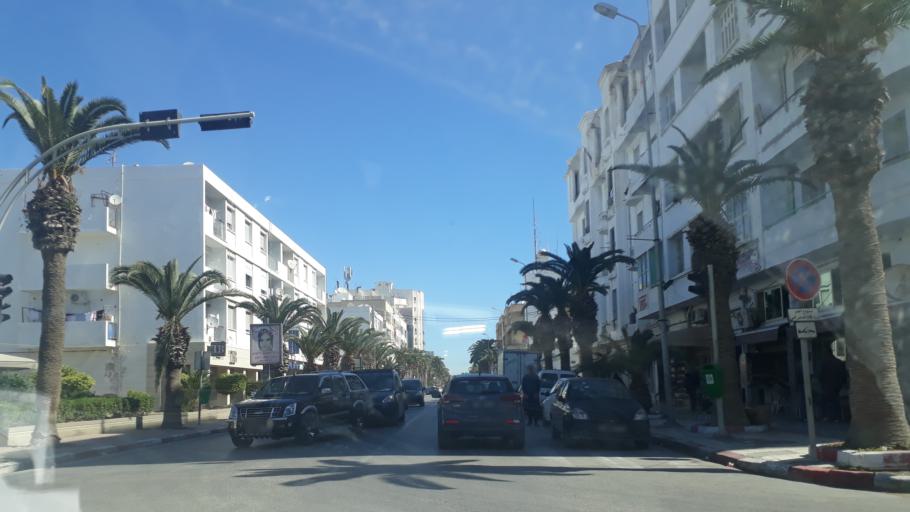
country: TN
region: Safaqis
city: Sfax
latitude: 34.7295
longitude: 10.7600
